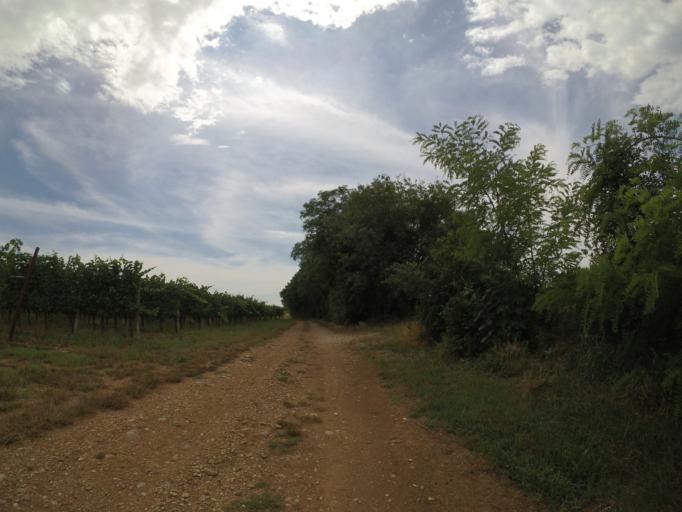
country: IT
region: Friuli Venezia Giulia
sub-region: Provincia di Udine
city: Bertiolo
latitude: 45.9610
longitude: 13.0582
